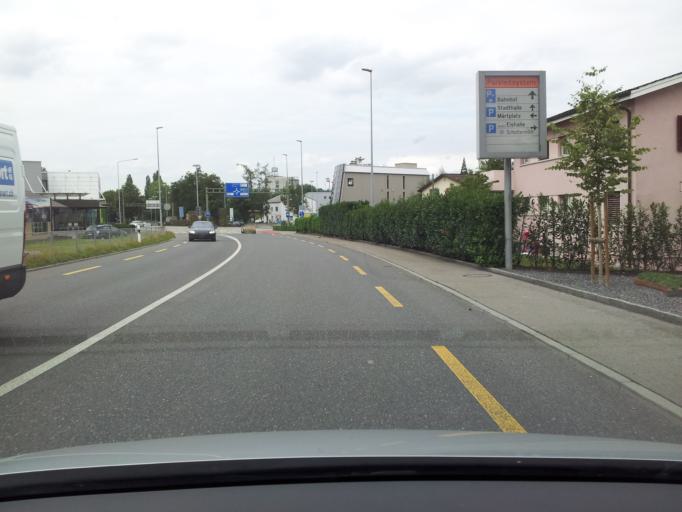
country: CH
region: Lucerne
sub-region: Sursee District
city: Sursee
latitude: 47.1753
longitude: 8.1109
